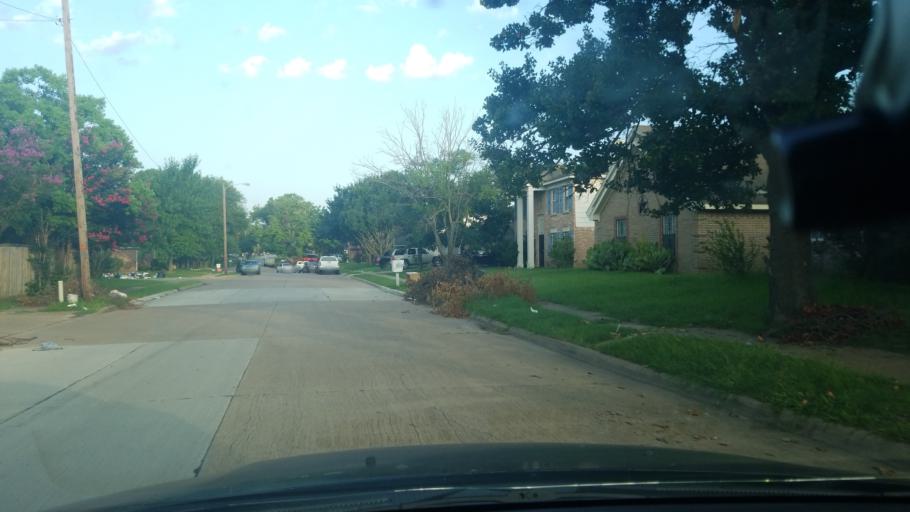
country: US
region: Texas
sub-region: Dallas County
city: Balch Springs
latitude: 32.7290
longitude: -96.6522
